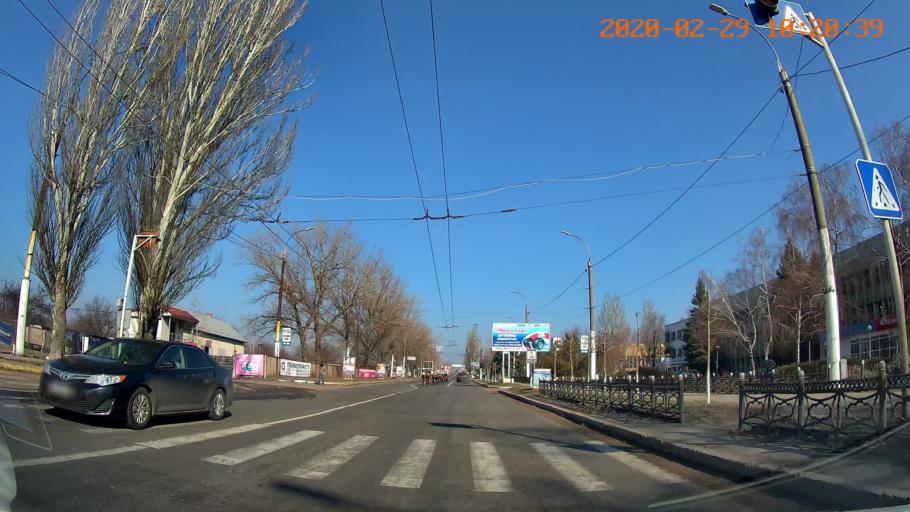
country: MD
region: Telenesti
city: Tiraspolul Nou
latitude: 46.8621
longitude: 29.6102
